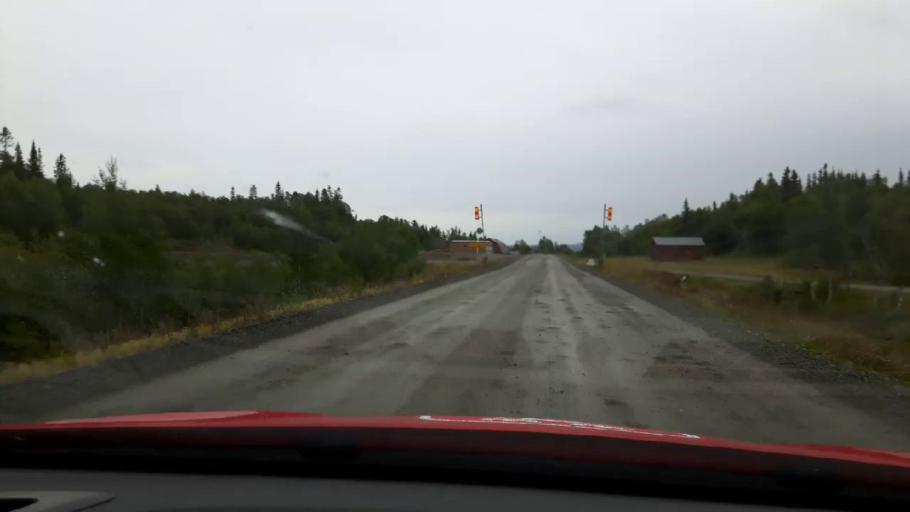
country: NO
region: Nord-Trondelag
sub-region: Meraker
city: Meraker
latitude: 63.5707
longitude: 12.2822
